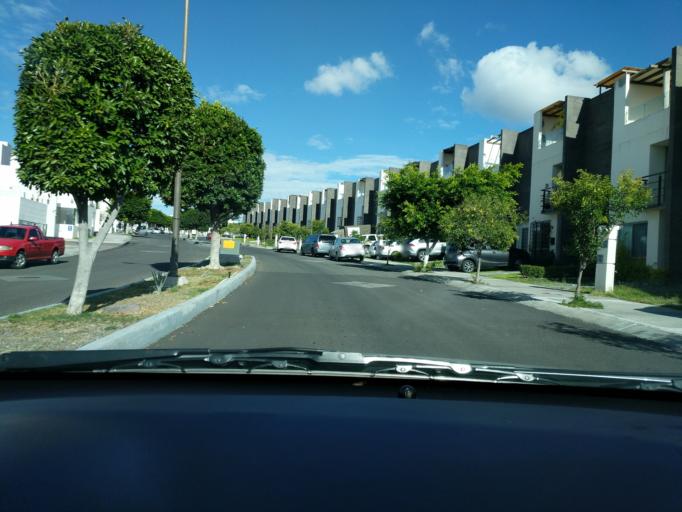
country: MX
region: Queretaro
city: La Canada
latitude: 20.5854
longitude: -100.3378
